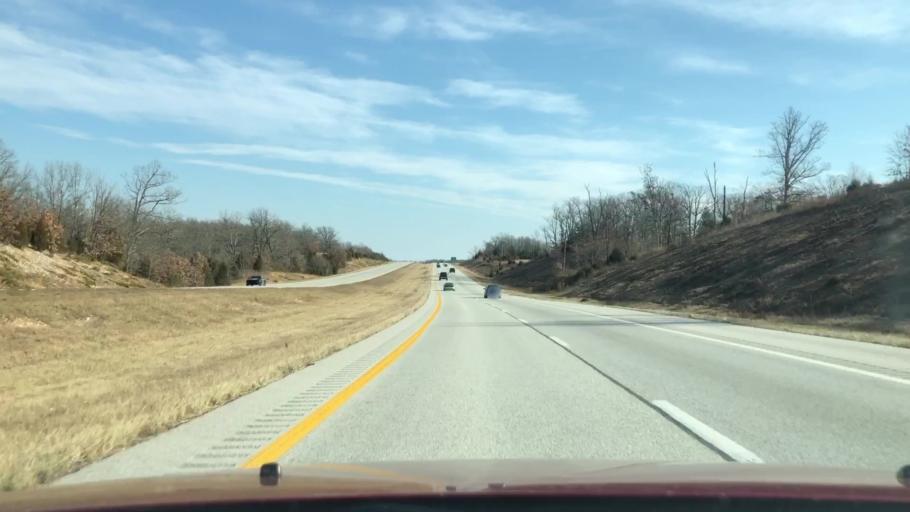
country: US
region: Missouri
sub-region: Webster County
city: Seymour
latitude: 37.1610
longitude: -92.8931
